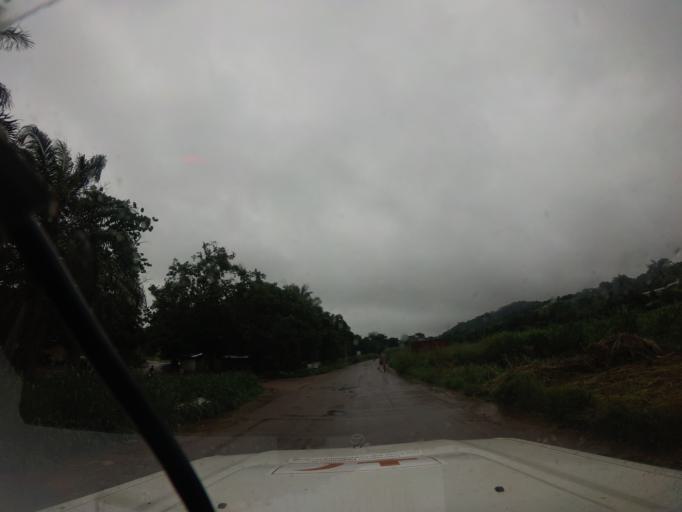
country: SL
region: Northern Province
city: Kabala
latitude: 9.5779
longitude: -11.5561
